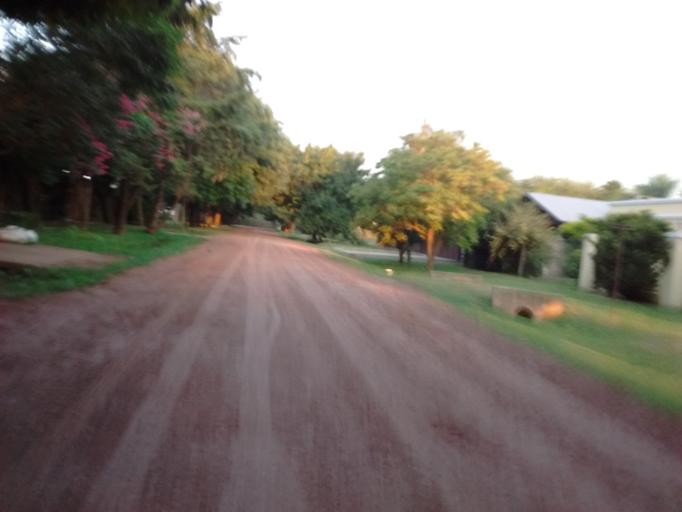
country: AR
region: Santa Fe
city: Funes
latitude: -32.9232
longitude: -60.8386
